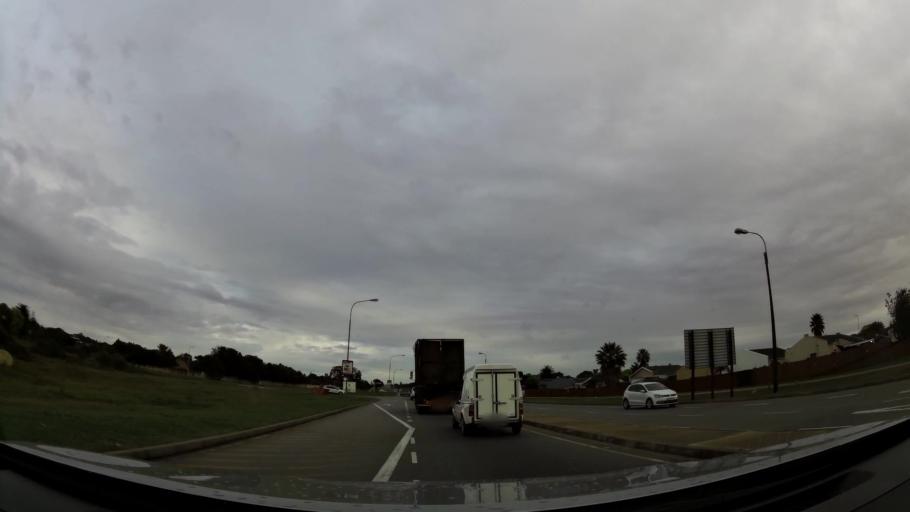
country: ZA
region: Eastern Cape
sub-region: Nelson Mandela Bay Metropolitan Municipality
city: Port Elizabeth
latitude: -33.9917
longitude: 25.5506
